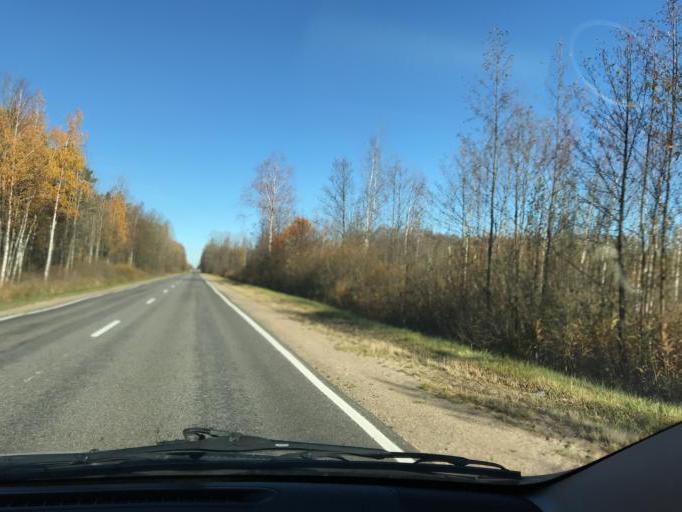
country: BY
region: Vitebsk
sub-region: Ushatski Rayon
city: Ushachy
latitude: 55.0736
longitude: 28.7543
